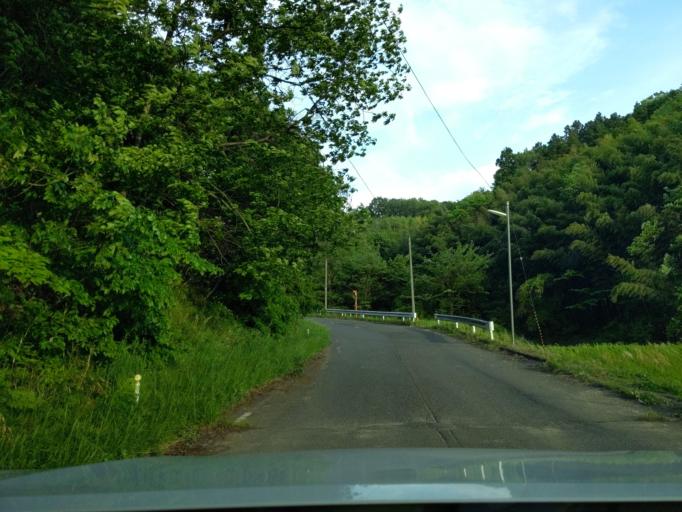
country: JP
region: Fukushima
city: Miharu
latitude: 37.4134
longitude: 140.4655
